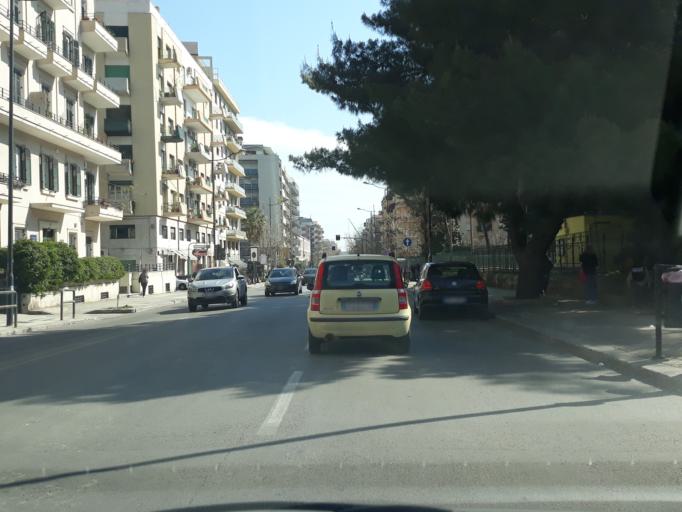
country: IT
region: Sicily
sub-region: Palermo
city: Palermo
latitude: 38.1341
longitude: 13.3506
